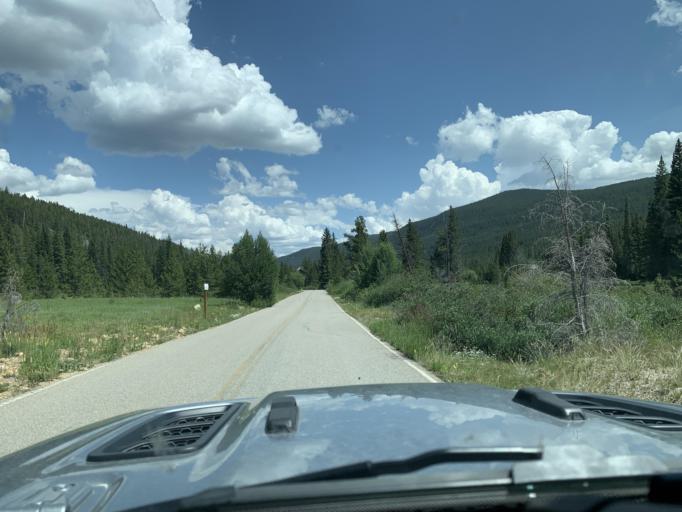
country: US
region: Colorado
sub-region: Lake County
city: Leadville North
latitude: 39.2808
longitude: -106.4396
